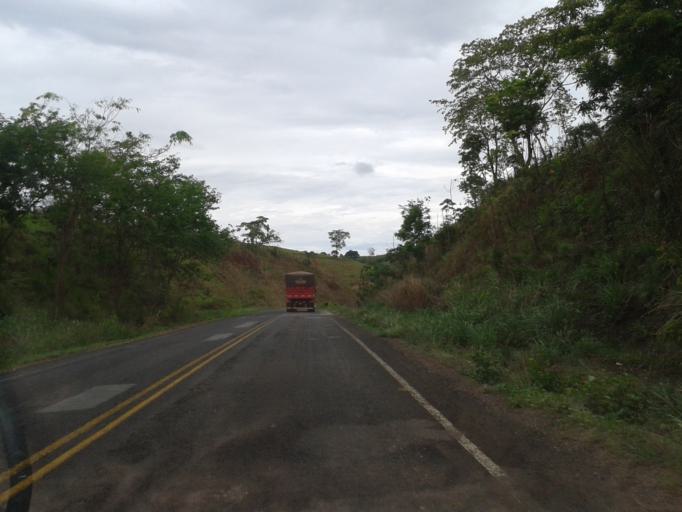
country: BR
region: Goias
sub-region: Caldas Novas
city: Caldas Novas
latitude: -18.0610
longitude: -48.6738
